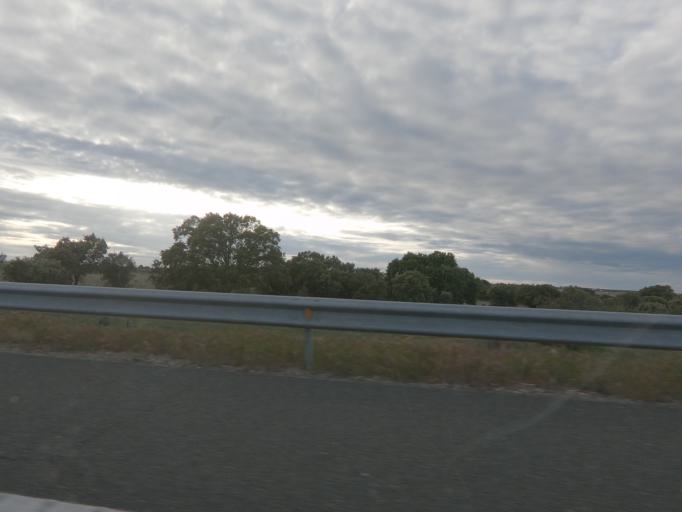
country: ES
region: Extremadura
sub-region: Provincia de Caceres
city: Casar de Caceres
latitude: 39.5099
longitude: -6.4335
